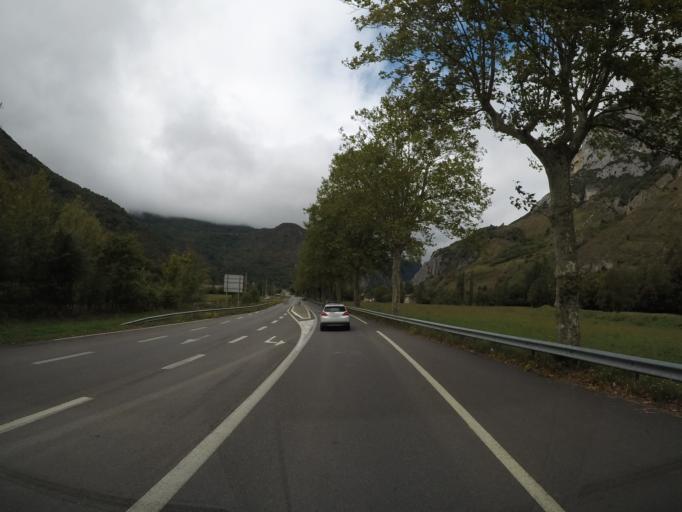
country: FR
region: Midi-Pyrenees
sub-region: Departement de l'Ariege
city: Tarascon-sur-Ariege
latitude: 42.7978
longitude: 1.6682
